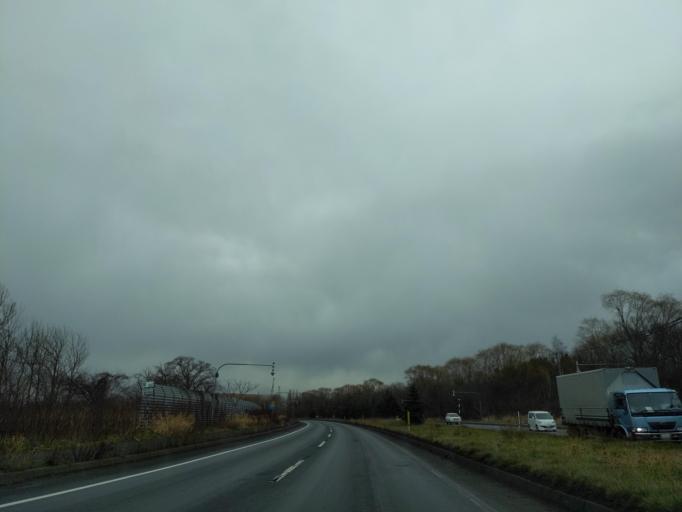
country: JP
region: Hokkaido
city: Ishikari
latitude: 43.1682
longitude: 141.4027
